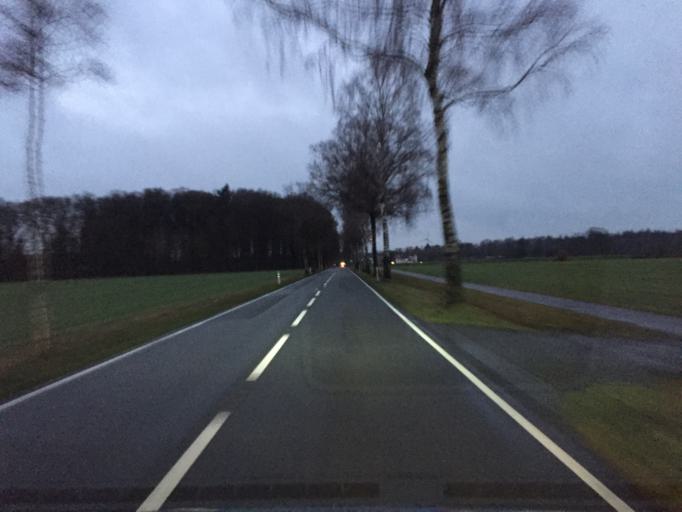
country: DE
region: Lower Saxony
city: Schwaforden
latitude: 52.7465
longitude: 8.8232
